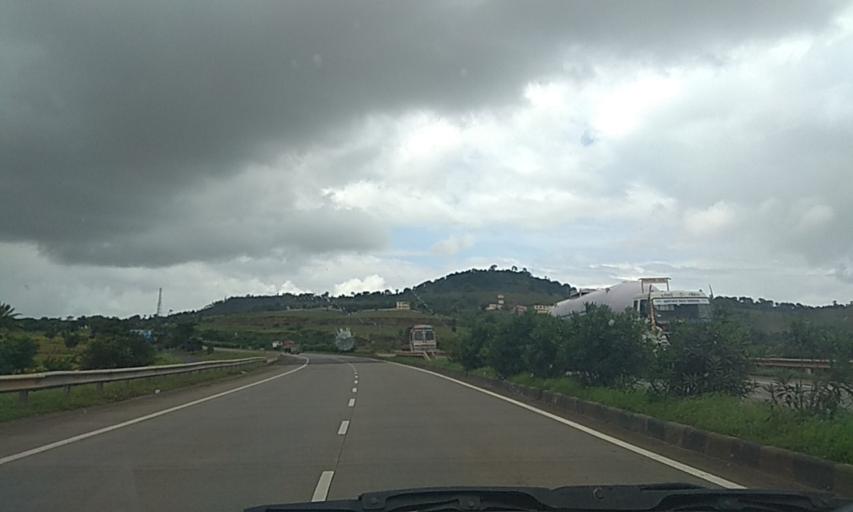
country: IN
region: Karnataka
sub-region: Belgaum
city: Sankeshwar
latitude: 16.2689
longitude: 74.4631
